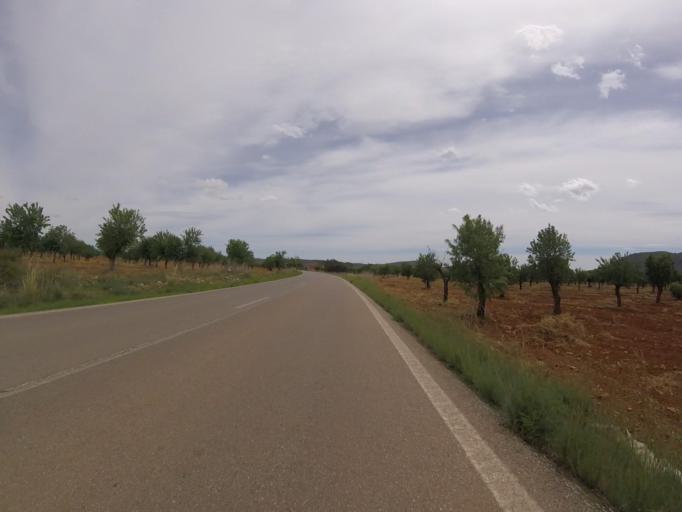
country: ES
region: Valencia
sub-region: Provincia de Castello
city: Cabanes
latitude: 40.1658
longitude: 0.0102
